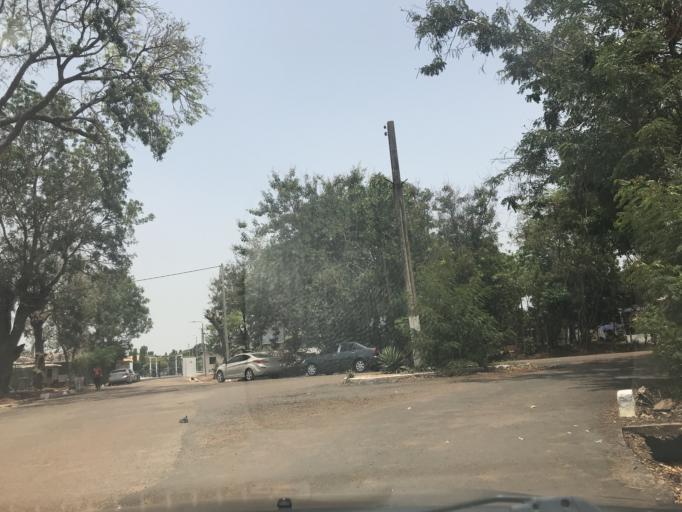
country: GH
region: Greater Accra
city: Accra
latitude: 5.5823
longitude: -0.1562
